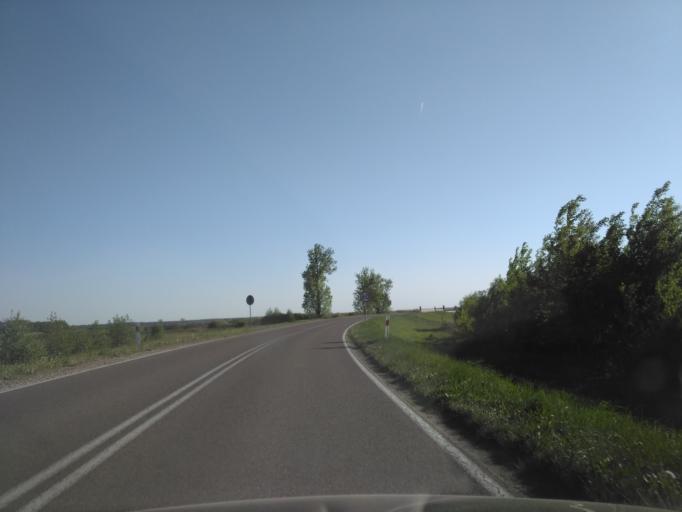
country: PL
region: Lublin Voivodeship
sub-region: Powiat swidnicki
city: Trawniki
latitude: 51.1787
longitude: 23.0509
